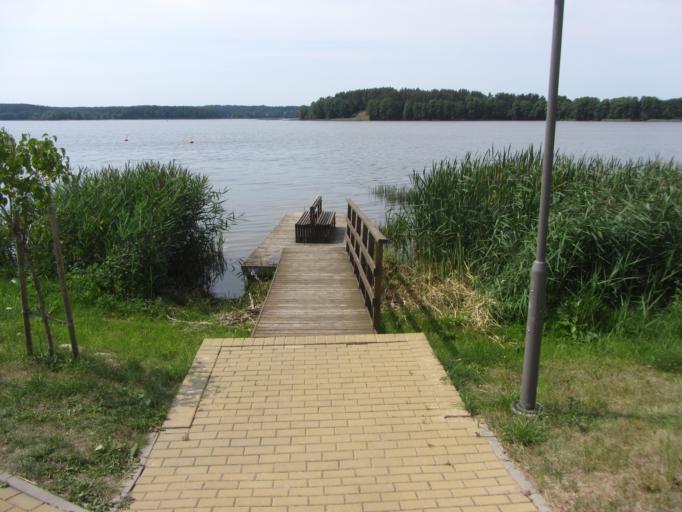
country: LT
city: Zarasai
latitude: 55.7348
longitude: 26.2403
